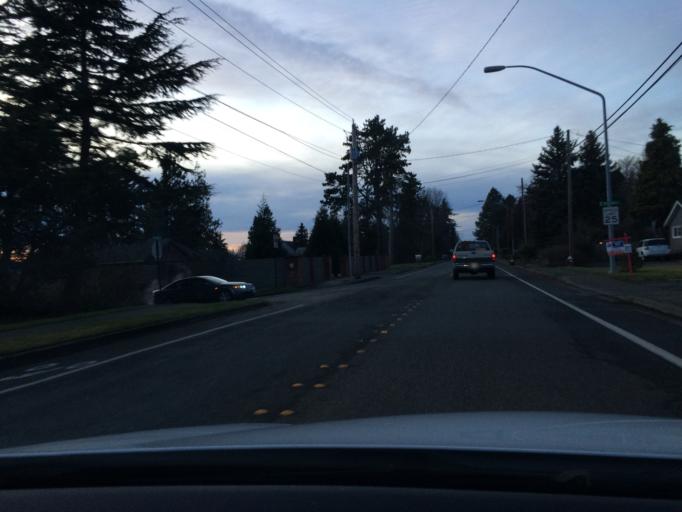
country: US
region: Washington
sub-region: Whatcom County
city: Bellingham
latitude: 48.7634
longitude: -122.5094
